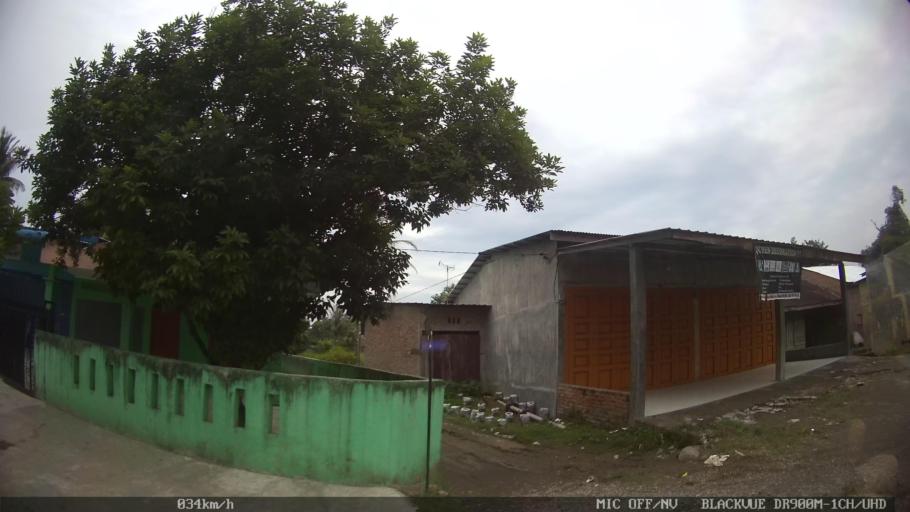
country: ID
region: North Sumatra
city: Binjai
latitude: 3.6428
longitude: 98.5510
